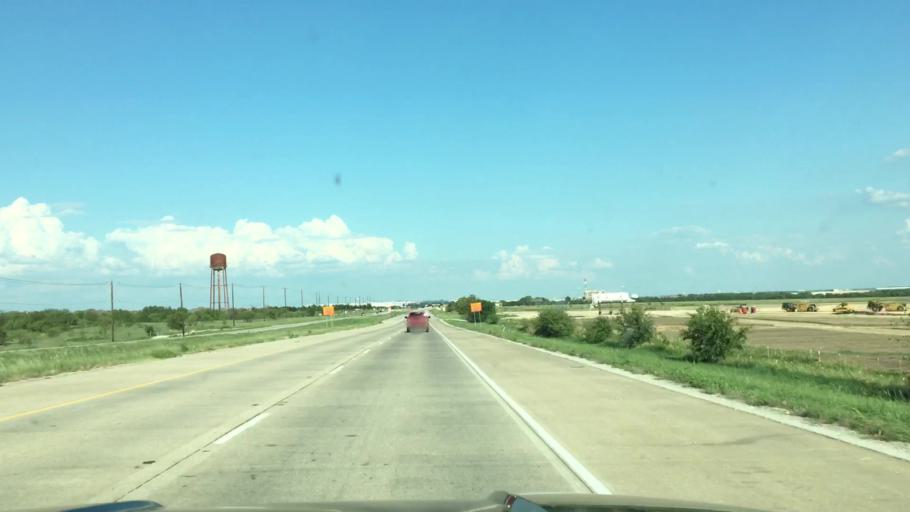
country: US
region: Texas
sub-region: Tarrant County
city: Haslet
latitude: 33.0352
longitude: -97.3393
